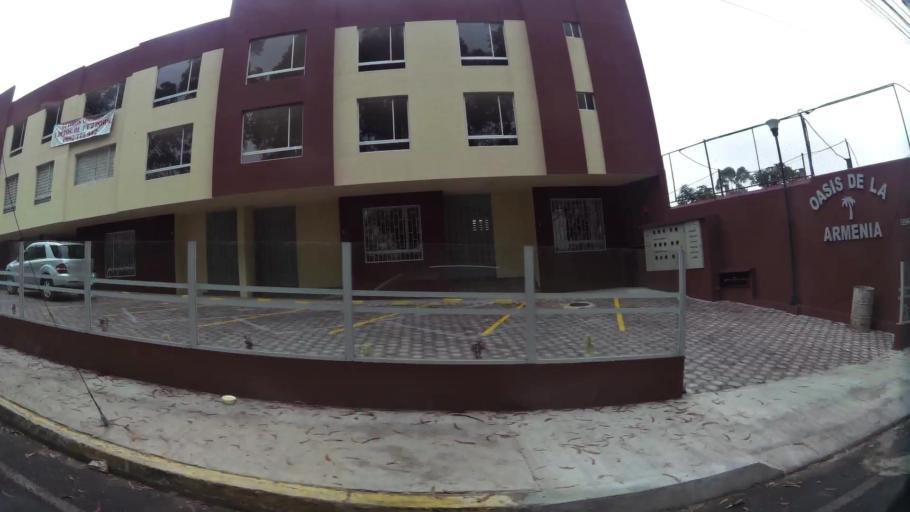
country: EC
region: Pichincha
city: Quito
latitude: -0.2664
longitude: -78.4728
